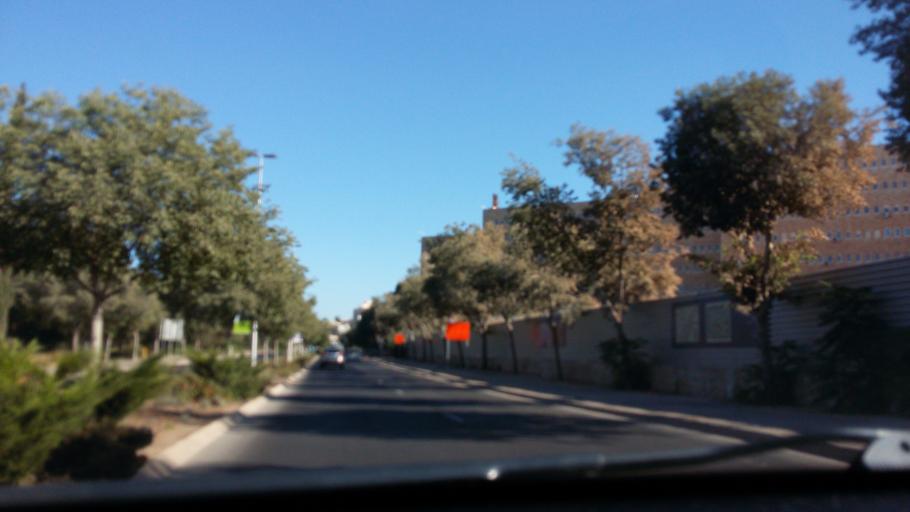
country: IL
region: Jerusalem
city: Jerusalem
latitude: 31.7763
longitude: 35.2031
